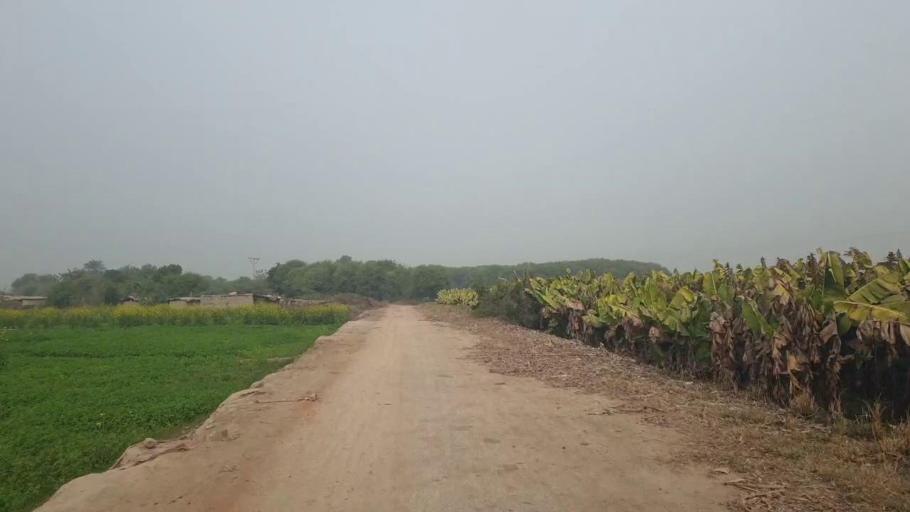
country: PK
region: Sindh
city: Tando Adam
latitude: 25.7158
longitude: 68.6156
